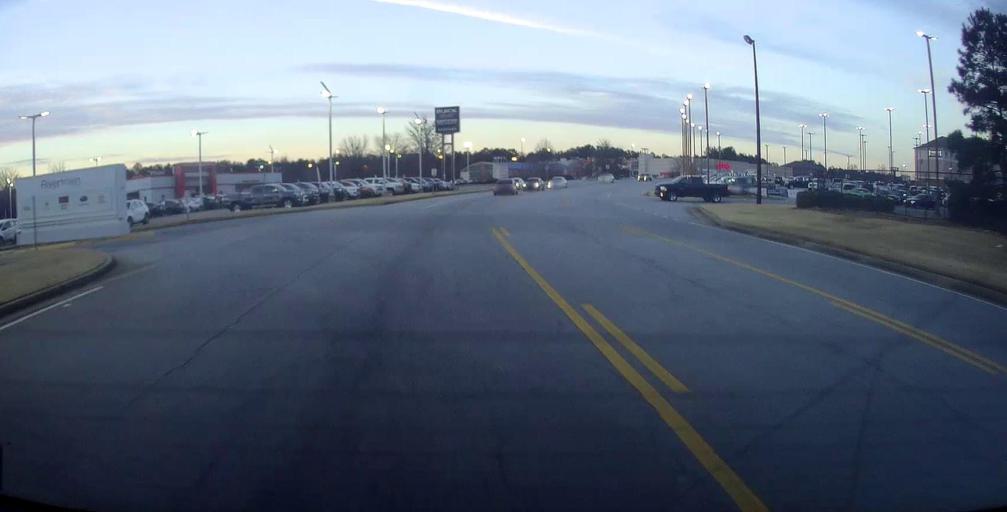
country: US
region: Alabama
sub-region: Russell County
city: Phenix City
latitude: 32.5373
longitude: -84.9692
